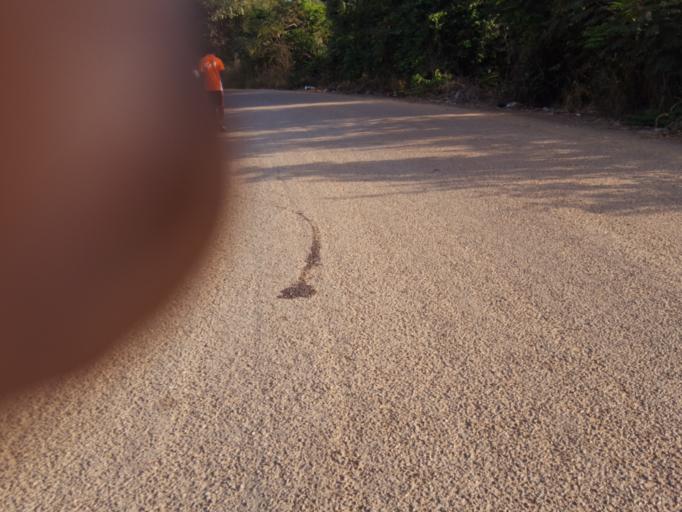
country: GH
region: Central
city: Cape Coast
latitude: 5.1133
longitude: -1.2913
